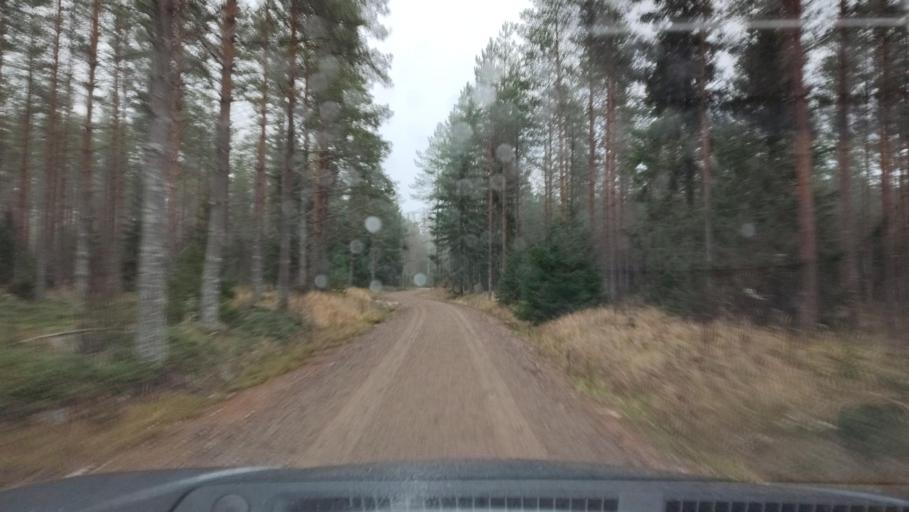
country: FI
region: Southern Ostrobothnia
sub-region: Suupohja
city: Karijoki
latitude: 62.1986
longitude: 21.7777
